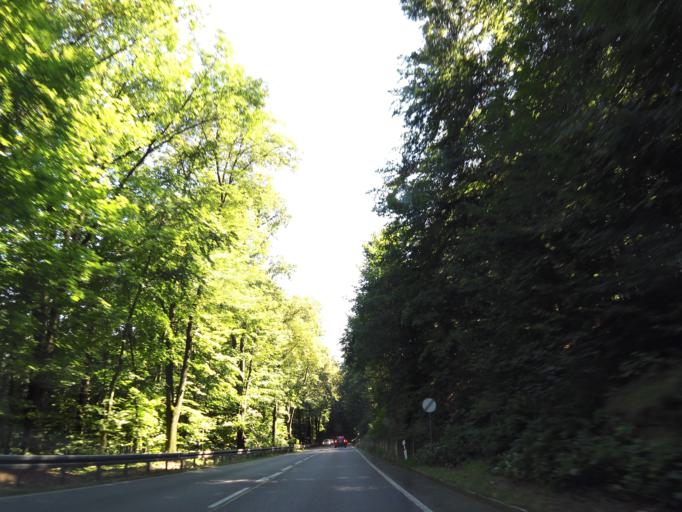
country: DE
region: Saxony
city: Konigstein
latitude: 50.9252
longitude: 14.0542
